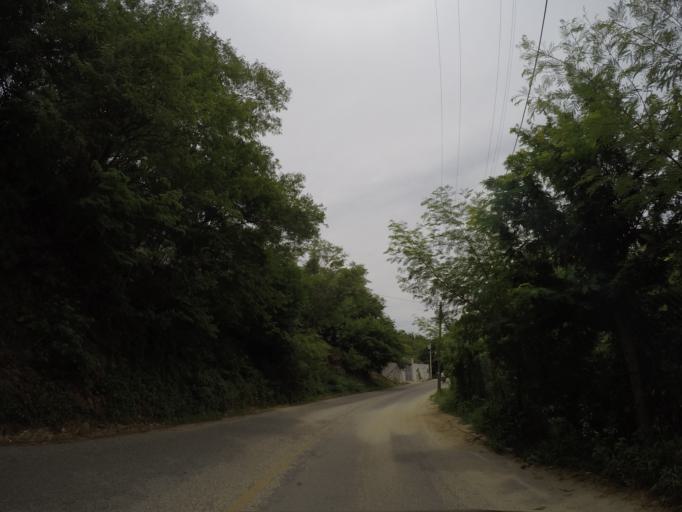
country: MX
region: Oaxaca
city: San Pedro Pochutla
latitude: 15.6675
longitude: -96.4972
